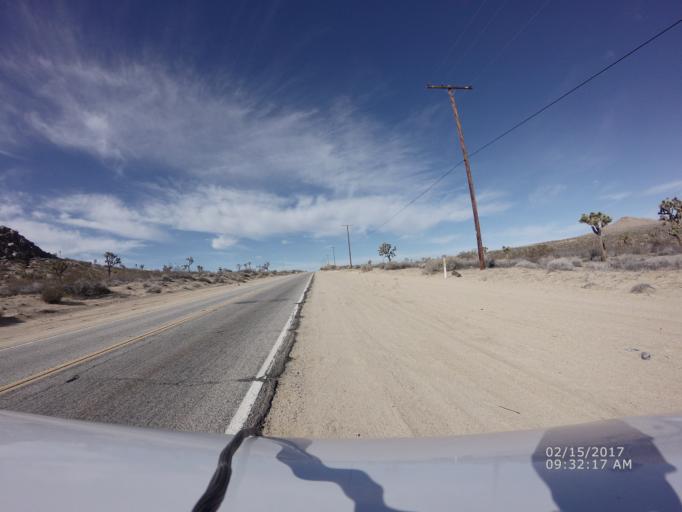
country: US
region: California
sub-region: Los Angeles County
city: Lake Los Angeles
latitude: 34.6167
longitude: -117.8869
